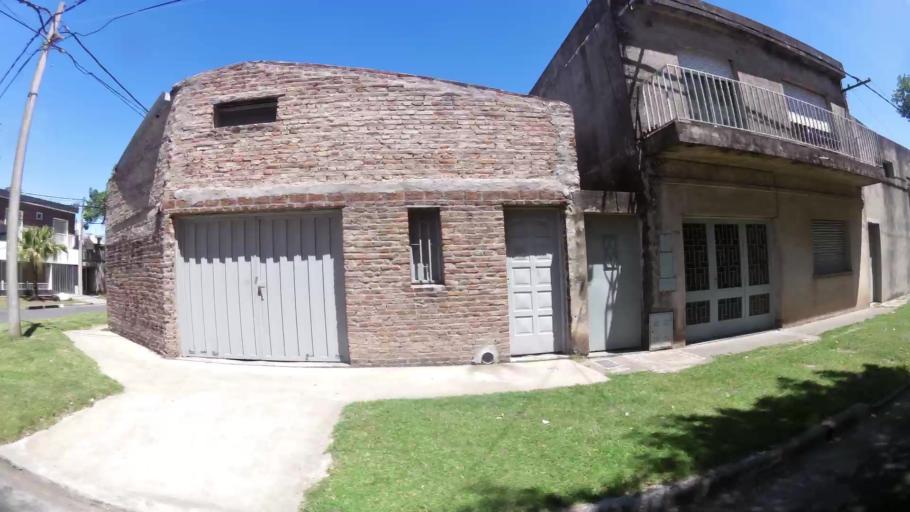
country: AR
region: Santa Fe
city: Perez
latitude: -32.9457
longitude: -60.7159
